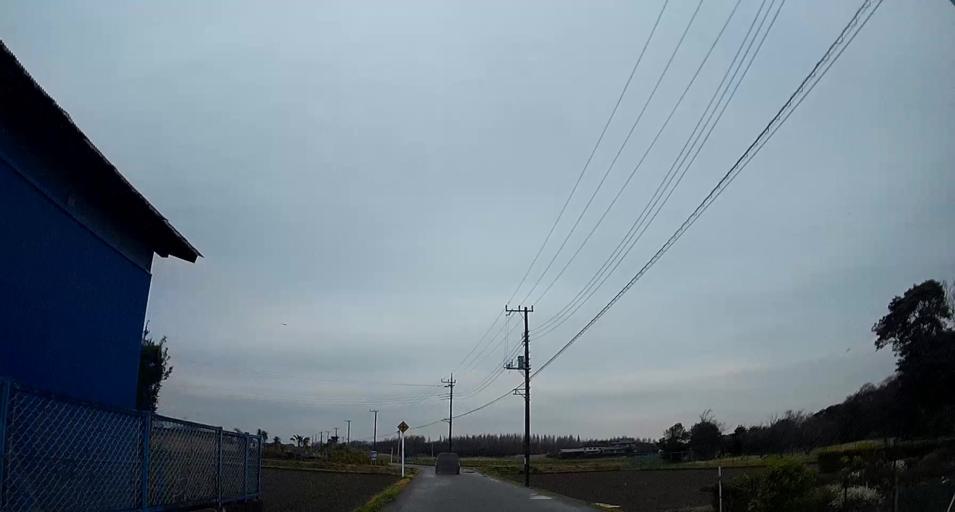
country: JP
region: Chiba
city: Kisarazu
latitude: 35.4131
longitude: 139.9180
